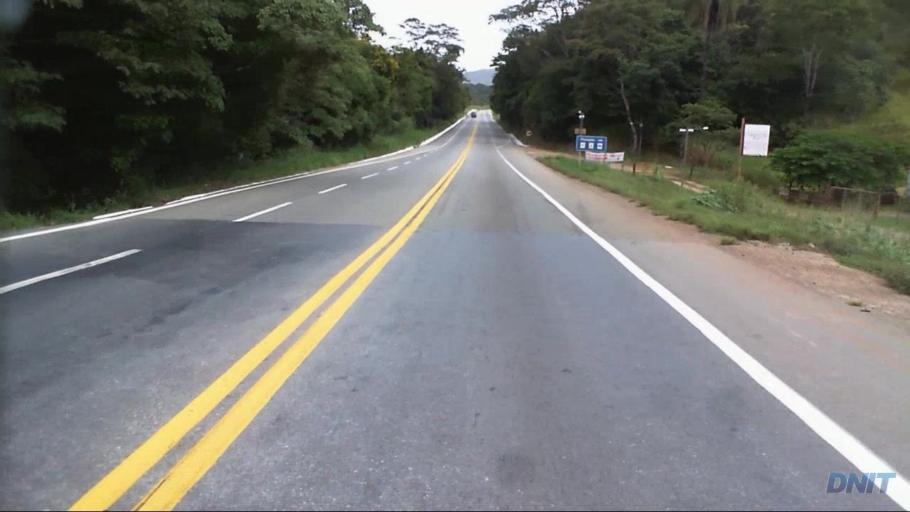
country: BR
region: Minas Gerais
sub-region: Santa Luzia
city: Santa Luzia
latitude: -19.7945
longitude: -43.7472
